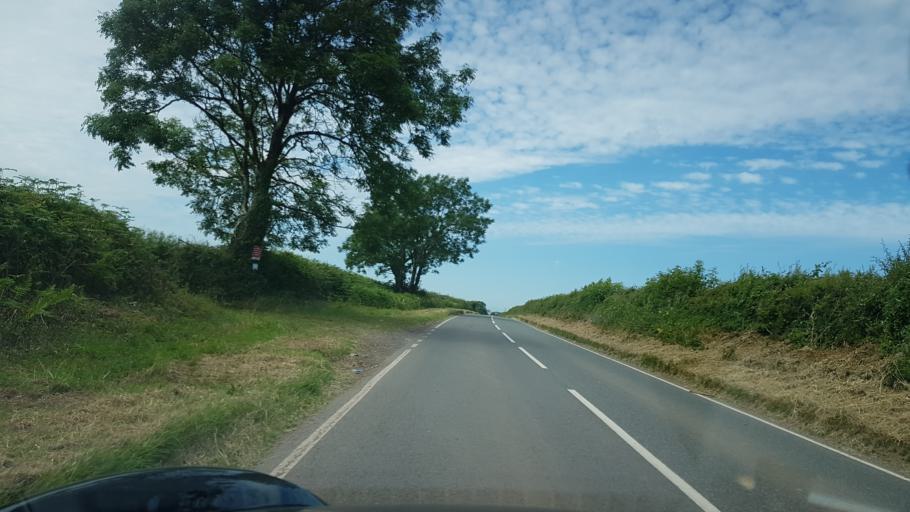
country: GB
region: Wales
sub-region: Carmarthenshire
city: Llanddowror
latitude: 51.7658
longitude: -4.5801
